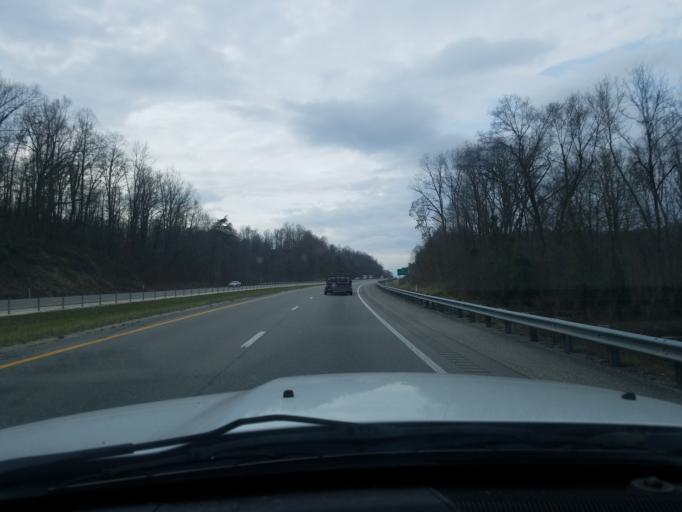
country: US
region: Kentucky
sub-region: Carter County
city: Olive Hill
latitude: 38.3227
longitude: -83.0890
